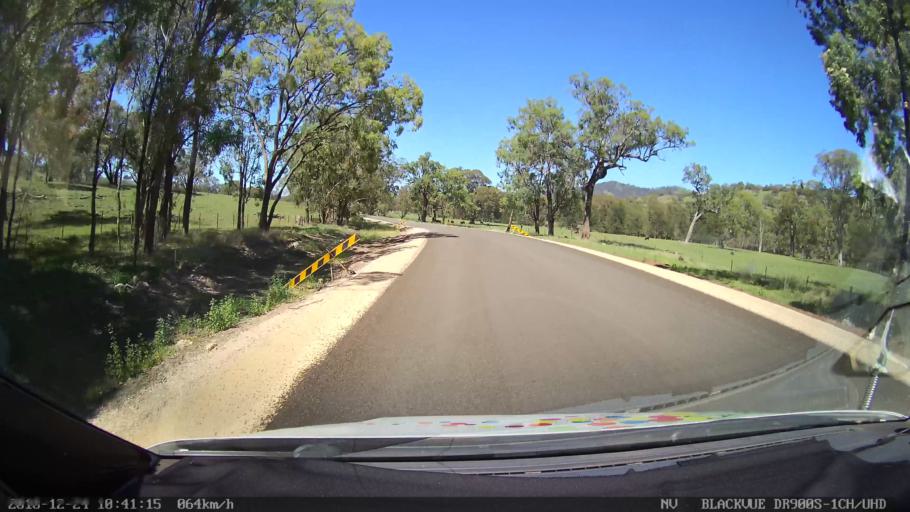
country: AU
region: New South Wales
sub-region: Upper Hunter Shire
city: Merriwa
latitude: -31.8674
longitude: 150.4606
